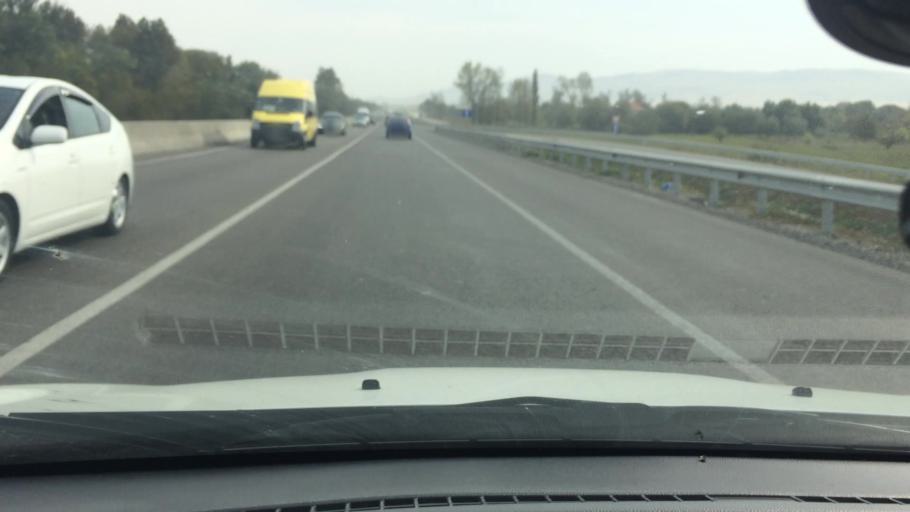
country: GE
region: Kvemo Kartli
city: Rust'avi
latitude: 41.6277
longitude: 44.9226
